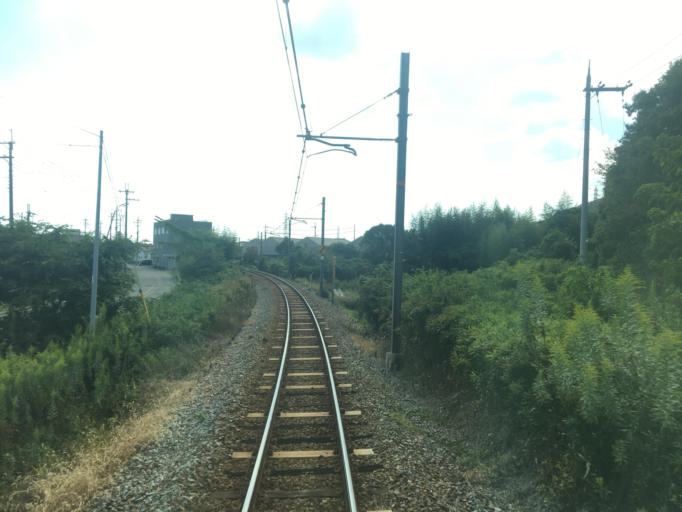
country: JP
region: Hyogo
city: Yashiro
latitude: 34.9506
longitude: 134.9636
